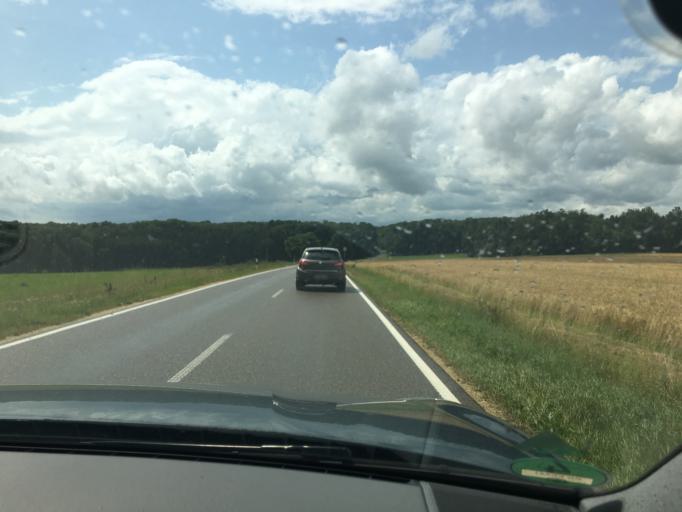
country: DE
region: Baden-Wuerttemberg
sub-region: Tuebingen Region
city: Nellingen
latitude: 48.5130
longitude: 9.7928
